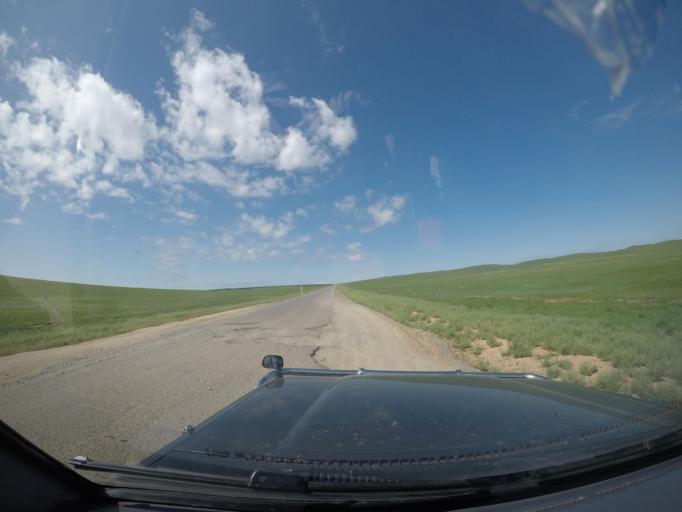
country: MN
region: Suhbaatar
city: Hanhohiy
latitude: 47.3838
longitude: 111.8493
